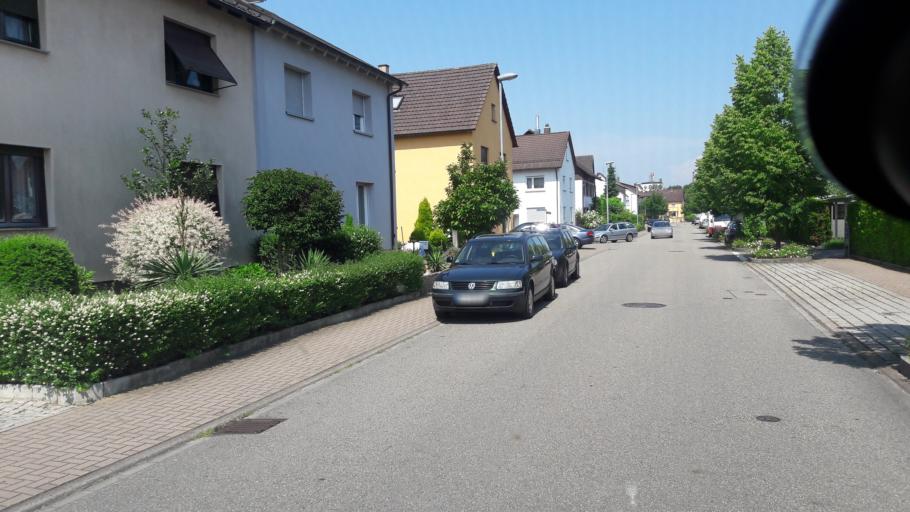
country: DE
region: Baden-Wuerttemberg
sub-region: Karlsruhe Region
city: Malsch
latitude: 48.8868
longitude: 8.3261
